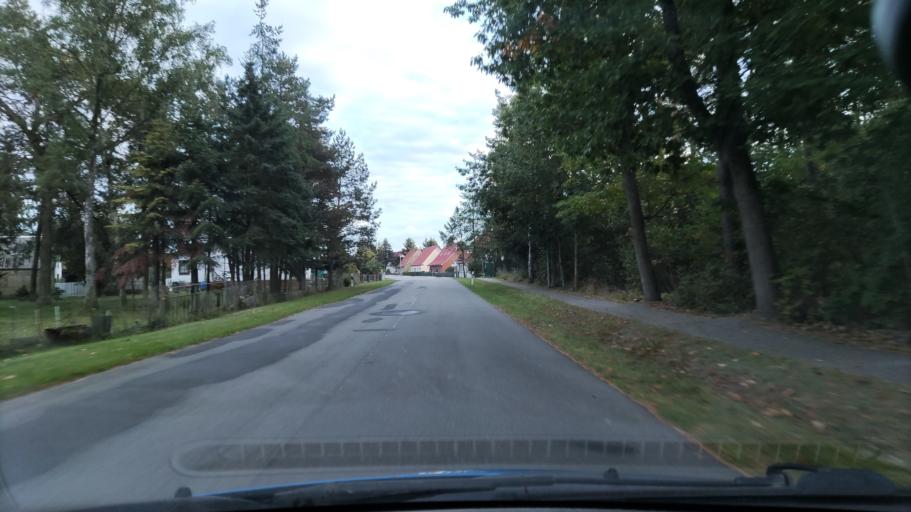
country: DE
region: Mecklenburg-Vorpommern
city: Boizenburg
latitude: 53.3719
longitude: 10.8579
